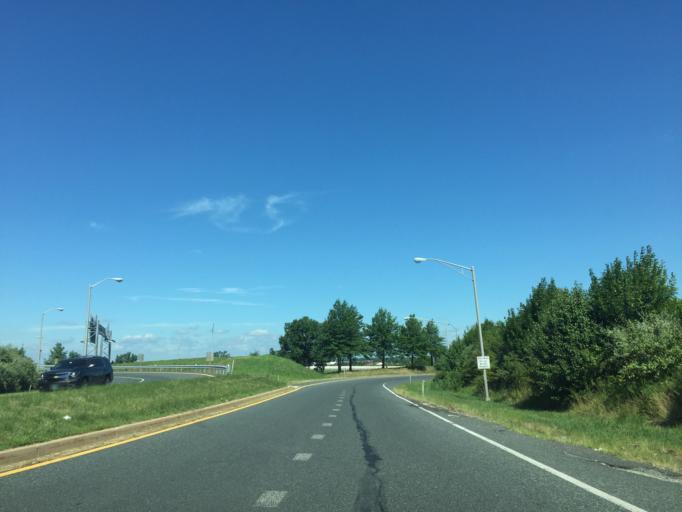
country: US
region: Maryland
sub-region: Baltimore County
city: Rosedale
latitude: 39.2926
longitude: -76.5515
